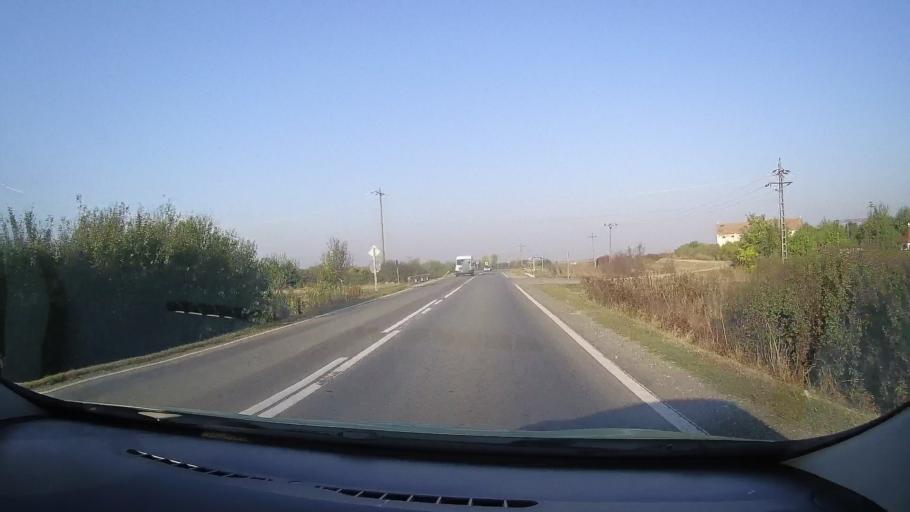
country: RO
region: Arad
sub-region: Comuna Socodor
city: Socodor
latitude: 46.5021
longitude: 21.4244
